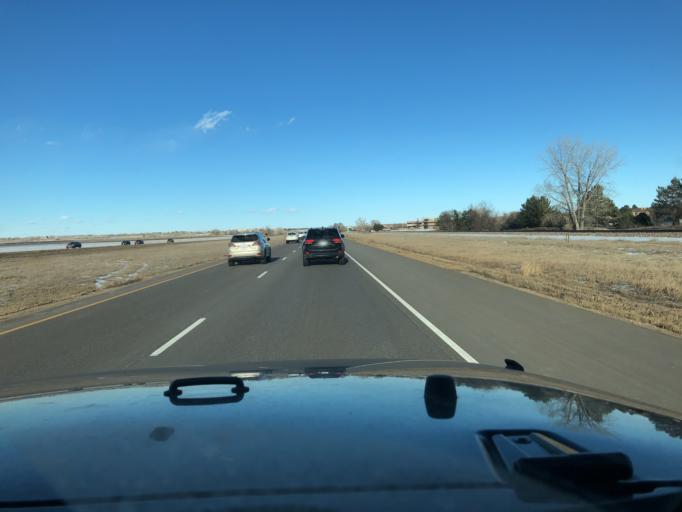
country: US
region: Colorado
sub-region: Boulder County
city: Gunbarrel
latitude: 40.0597
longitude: -105.2223
